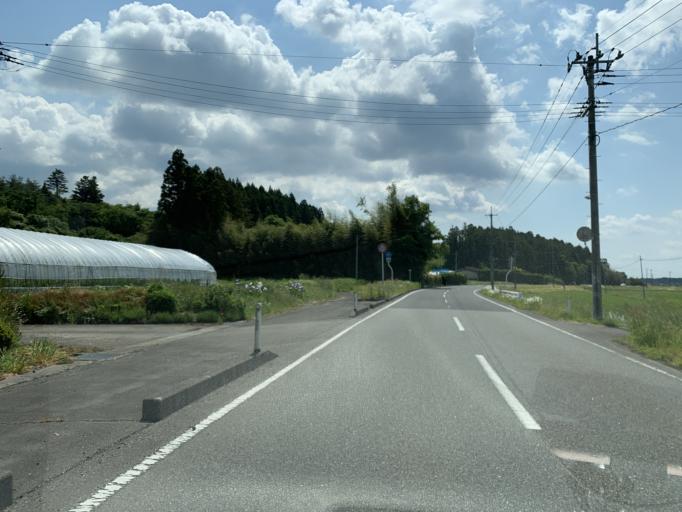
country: JP
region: Miyagi
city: Furukawa
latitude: 38.6859
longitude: 140.9724
